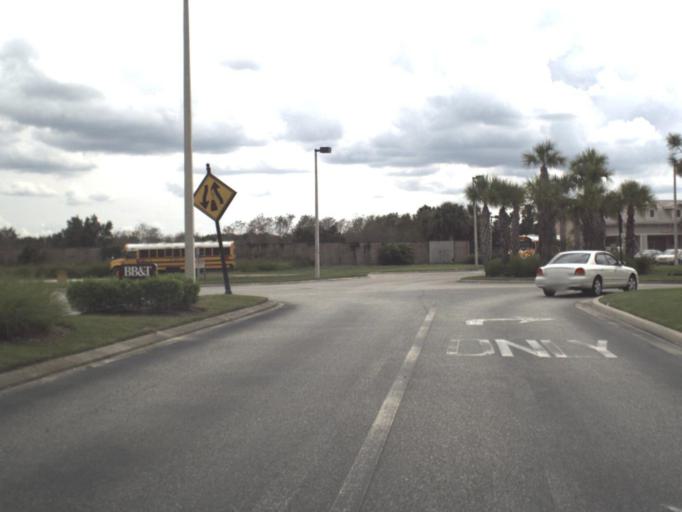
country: US
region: Florida
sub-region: Lee County
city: Fort Myers Shores
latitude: 26.7004
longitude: -81.7603
